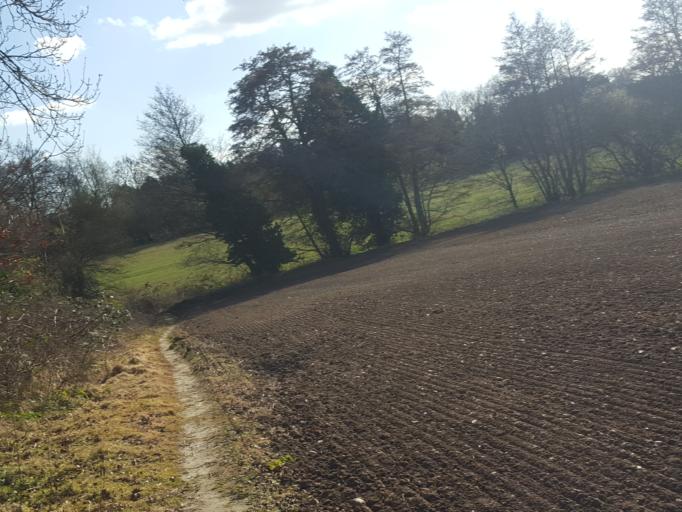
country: GB
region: England
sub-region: Essex
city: Little Clacton
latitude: 51.8637
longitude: 1.1137
